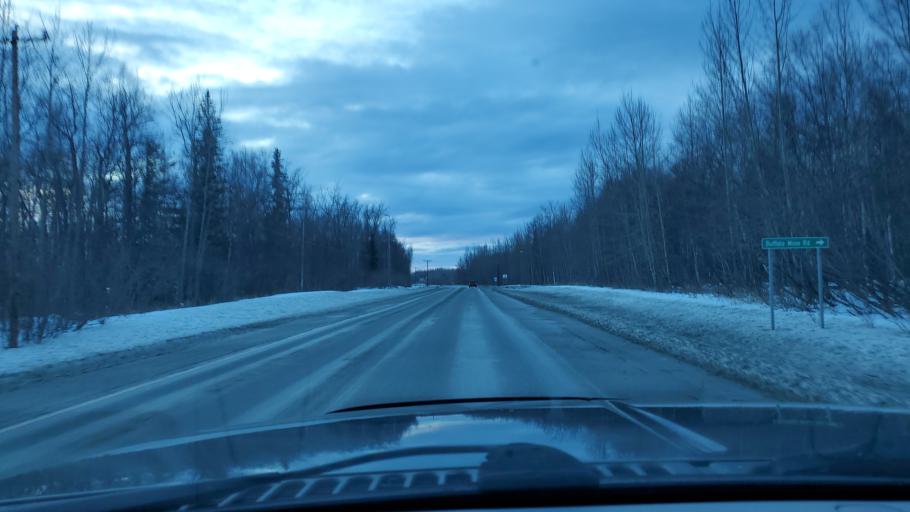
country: US
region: Alaska
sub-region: Matanuska-Susitna Borough
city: Farm Loop
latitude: 61.6703
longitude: -149.0736
